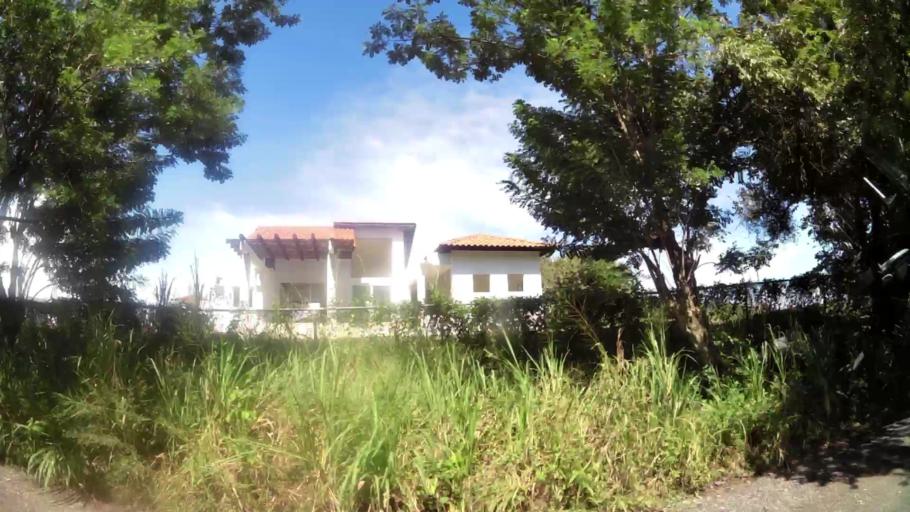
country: PA
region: Panama
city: Nueva Gorgona
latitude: 8.5581
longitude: -79.8616
